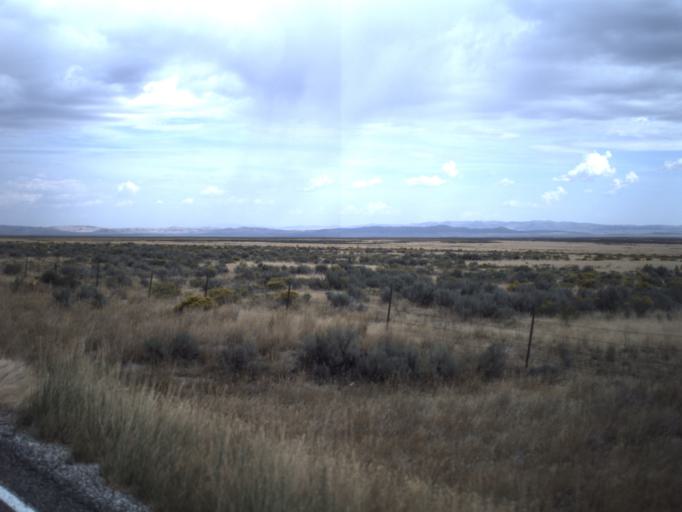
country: US
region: Idaho
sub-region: Oneida County
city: Malad City
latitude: 41.8975
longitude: -113.1082
